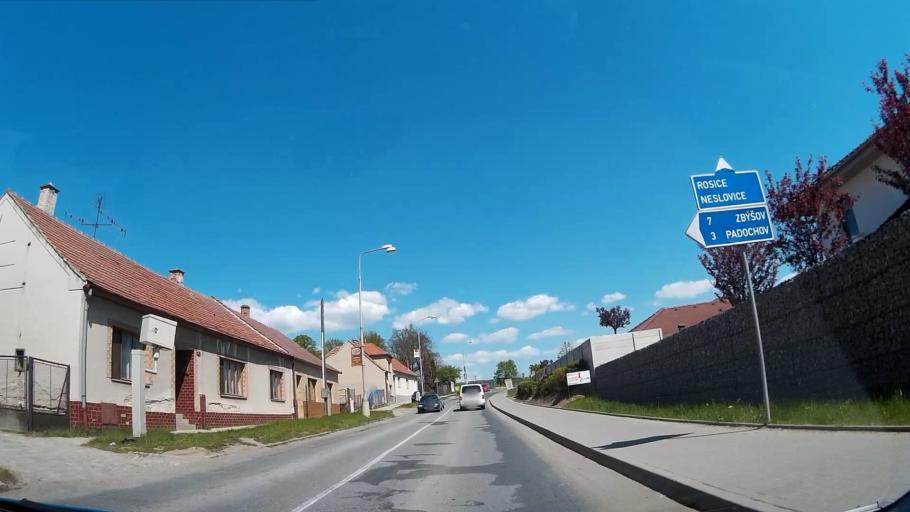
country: CZ
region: South Moravian
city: Ivancice
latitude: 49.1064
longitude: 16.3723
